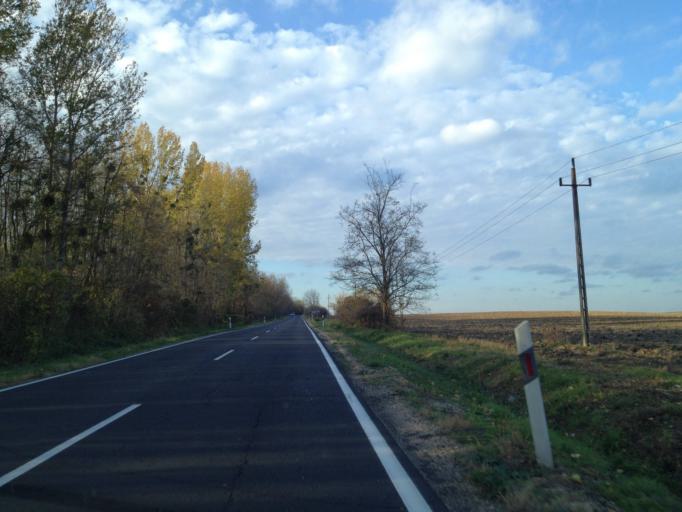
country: HU
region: Gyor-Moson-Sopron
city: Bakonyszentlaszlo
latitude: 47.4154
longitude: 17.8473
